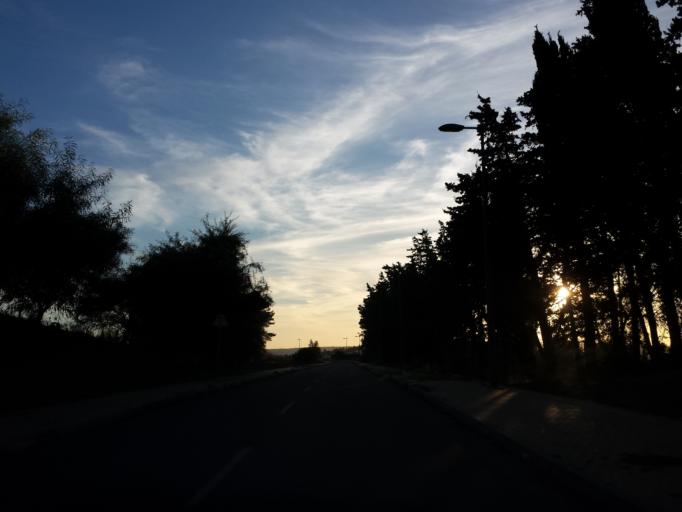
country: PT
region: Faro
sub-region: Lagos
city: Lagos
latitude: 37.1319
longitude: -8.6463
